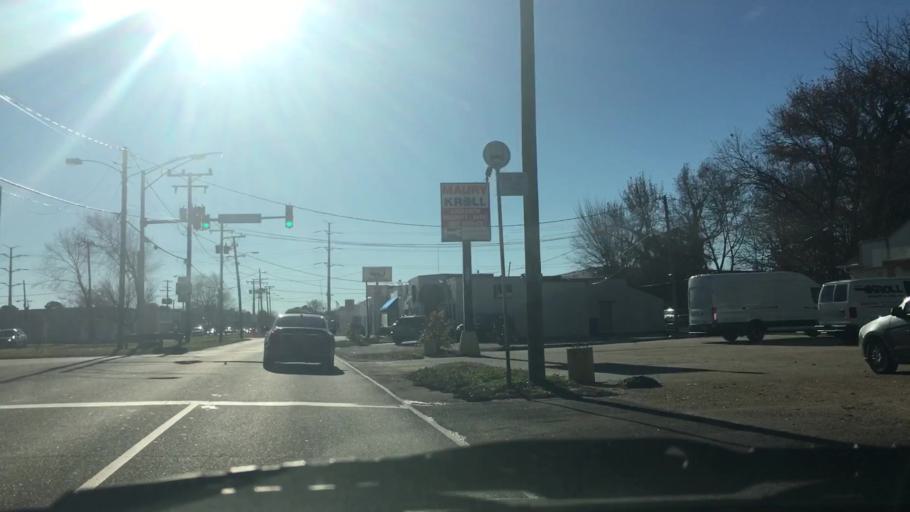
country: US
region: Virginia
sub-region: City of Norfolk
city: Norfolk
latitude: 36.8789
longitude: -76.2496
